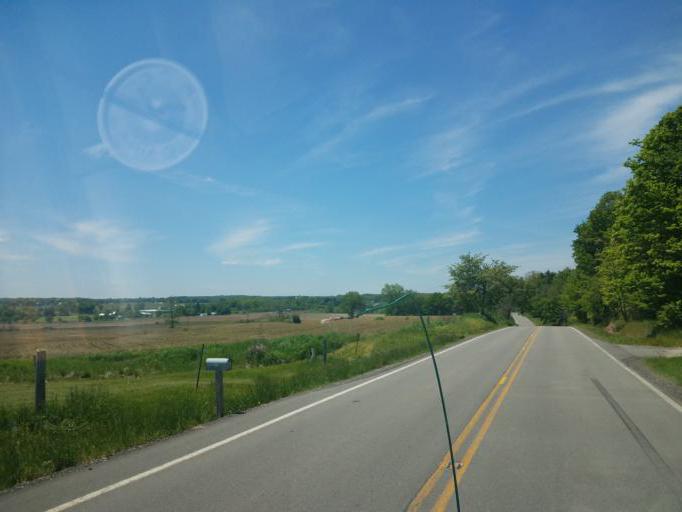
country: US
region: Ohio
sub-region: Ashland County
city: Ashland
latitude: 40.9602
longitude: -82.3534
